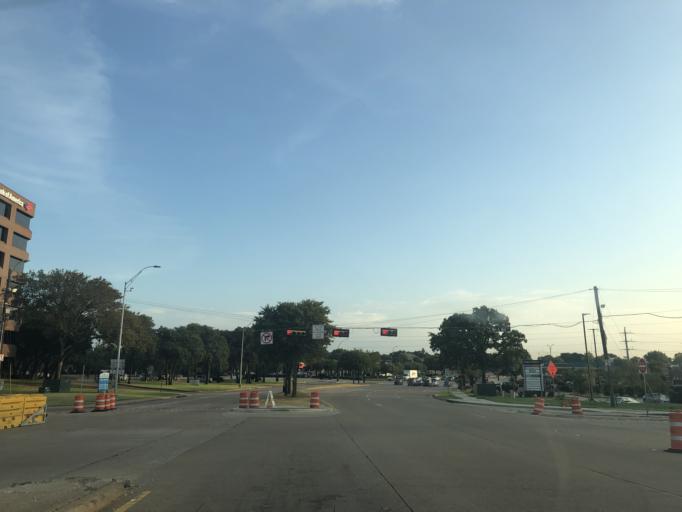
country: US
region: Texas
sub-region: Tarrant County
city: Arlington
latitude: 32.7610
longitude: -97.0759
